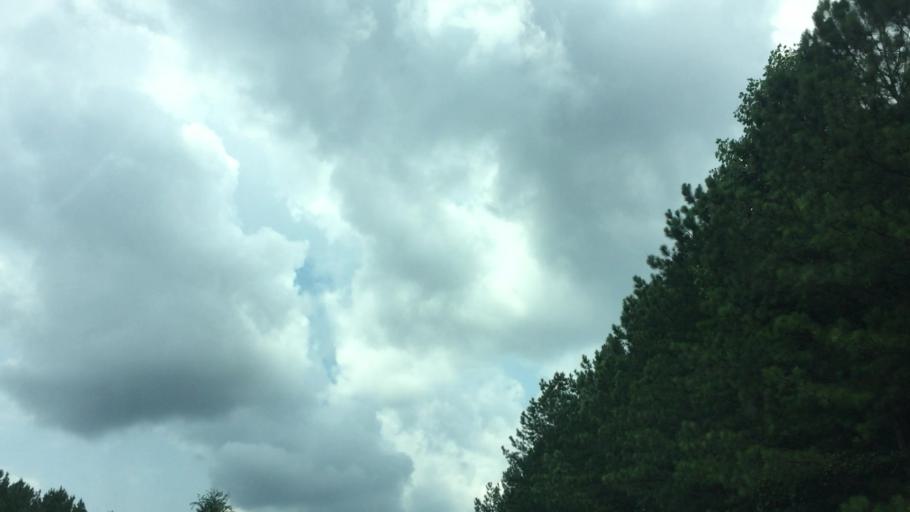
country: US
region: Georgia
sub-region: Fulton County
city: Palmetto
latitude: 33.5852
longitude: -84.6528
